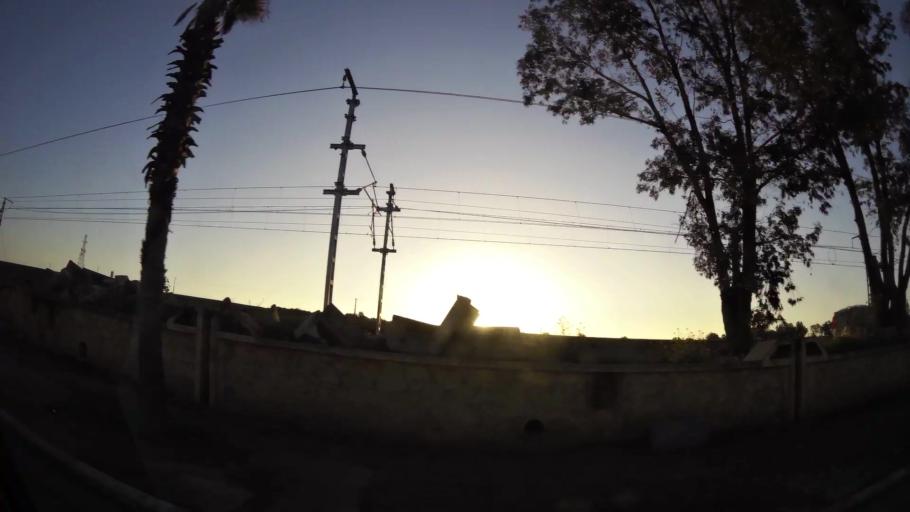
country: MA
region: Chaouia-Ouardigha
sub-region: Settat Province
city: Settat
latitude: 32.9880
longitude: -7.6209
